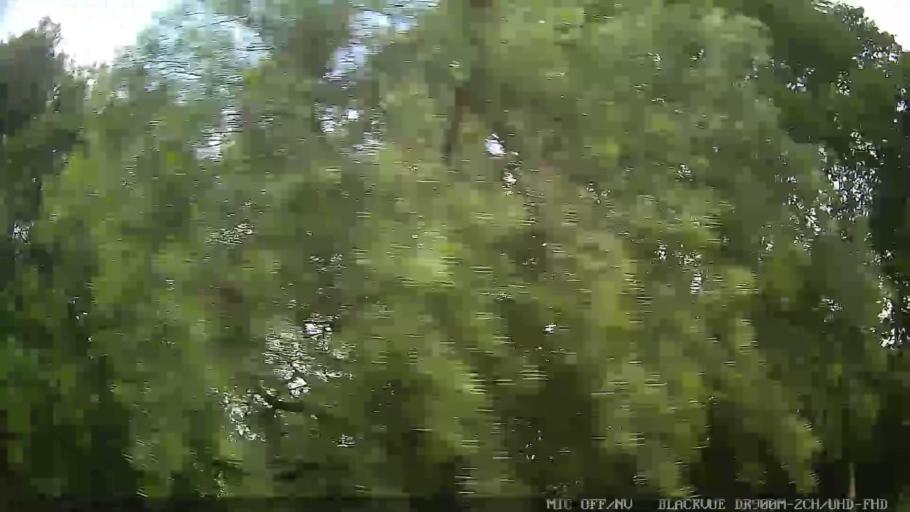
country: BR
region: Sao Paulo
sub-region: Louveira
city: Louveira
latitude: -23.1060
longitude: -46.9631
